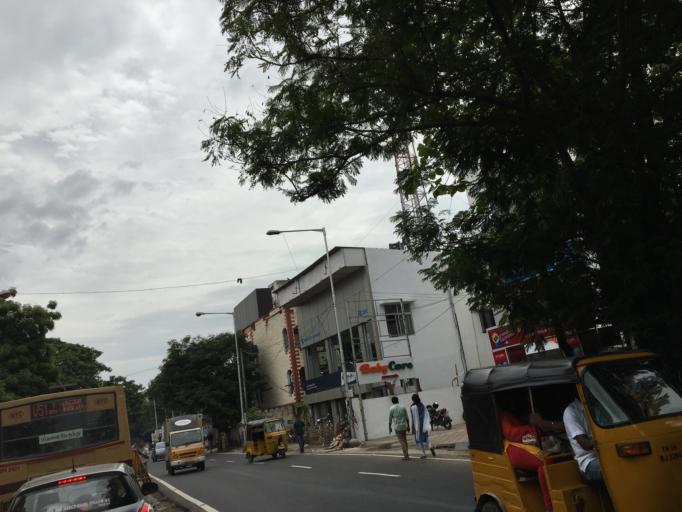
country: IN
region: Tamil Nadu
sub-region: Kancheepuram
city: Alandur
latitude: 12.9940
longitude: 80.2179
